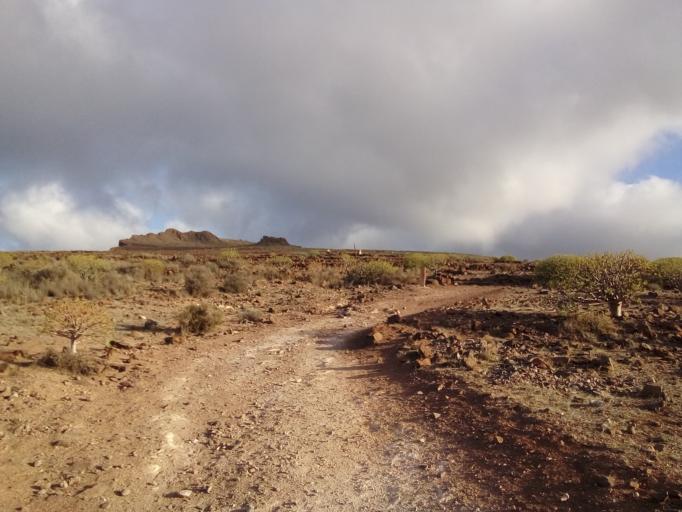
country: ES
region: Canary Islands
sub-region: Provincia de Santa Cruz de Tenerife
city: Vallehermosa
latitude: 28.1052
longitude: -17.3377
